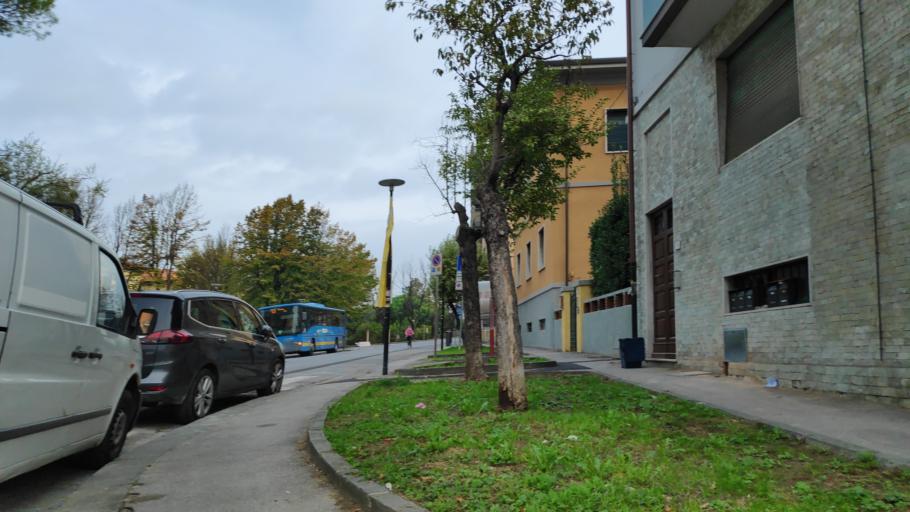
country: IT
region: Tuscany
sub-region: Province of Pisa
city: Pisa
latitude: 43.7047
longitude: 10.4014
